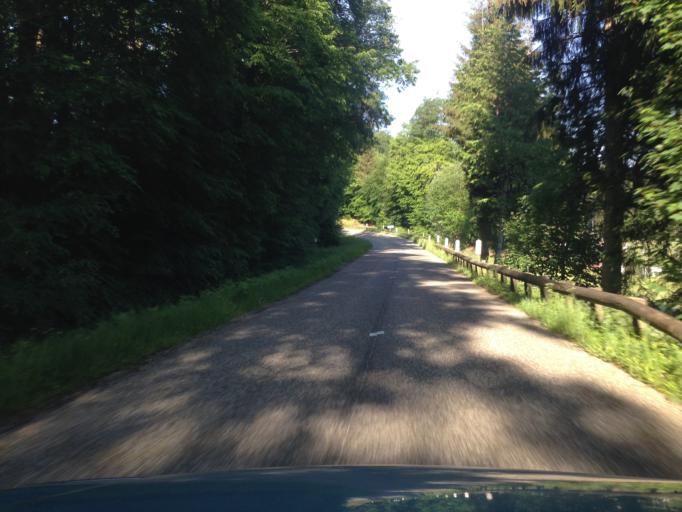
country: FR
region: Alsace
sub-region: Departement du Bas-Rhin
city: Wimmenau
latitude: 48.8754
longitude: 7.4016
